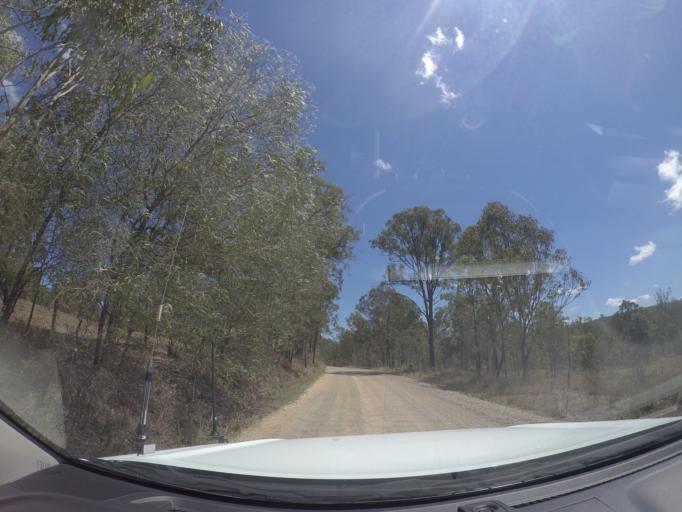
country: AU
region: Queensland
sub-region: Logan
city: North Maclean
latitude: -27.8300
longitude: 152.8655
